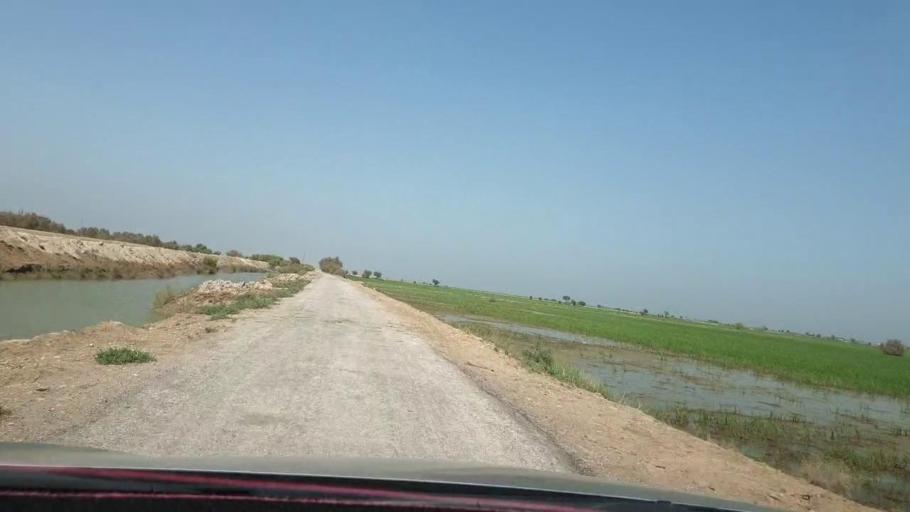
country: PK
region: Sindh
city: Warah
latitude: 27.5556
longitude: 67.7402
